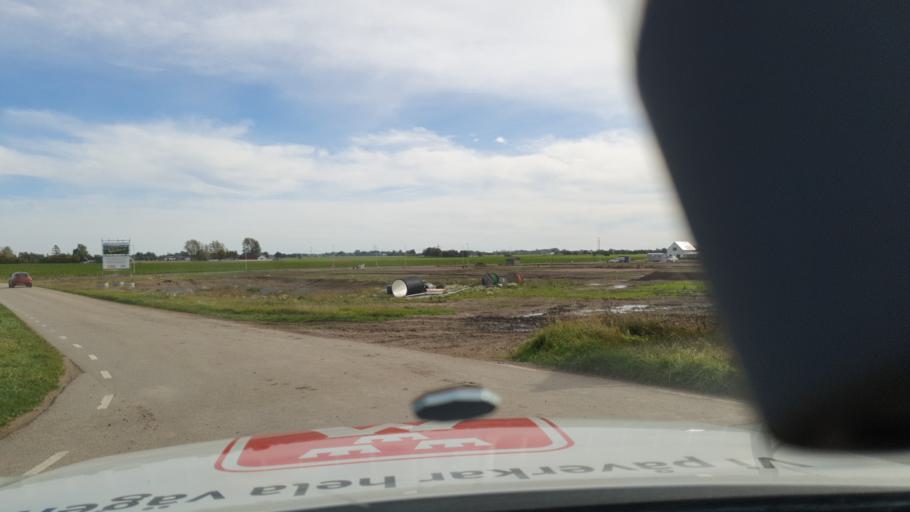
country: SE
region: Skane
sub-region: Vellinge Kommun
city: Vellinge
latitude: 55.4831
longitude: 13.0457
